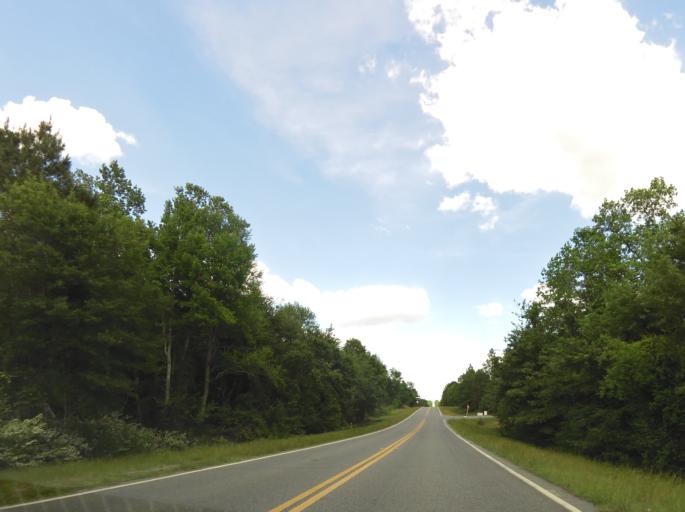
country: US
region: Georgia
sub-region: Telfair County
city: Helena
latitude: 32.2248
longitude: -82.9969
